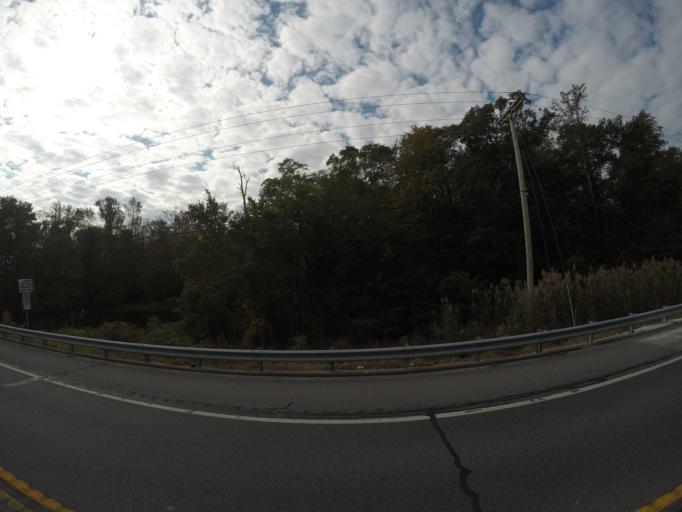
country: US
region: Delaware
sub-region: Sussex County
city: Bridgeville
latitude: 38.7090
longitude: -75.5219
